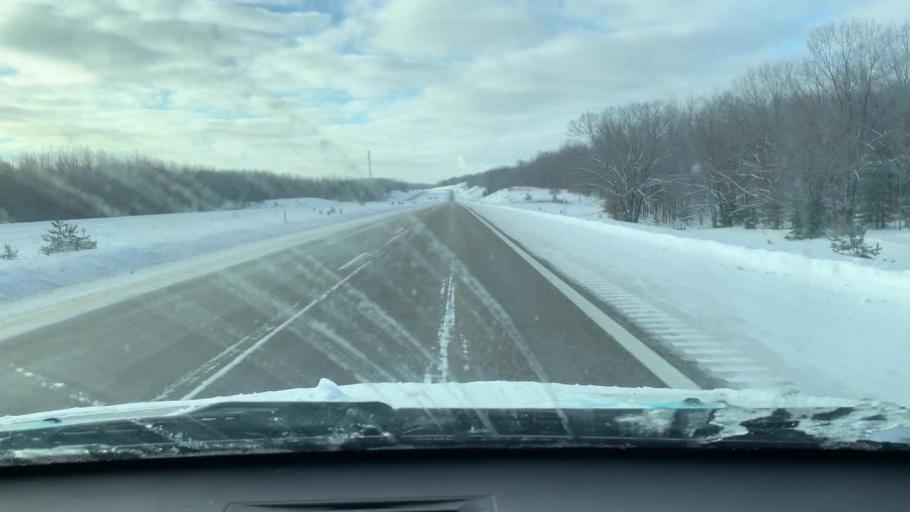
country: US
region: Michigan
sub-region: Wexford County
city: Manton
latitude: 44.3473
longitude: -85.4049
